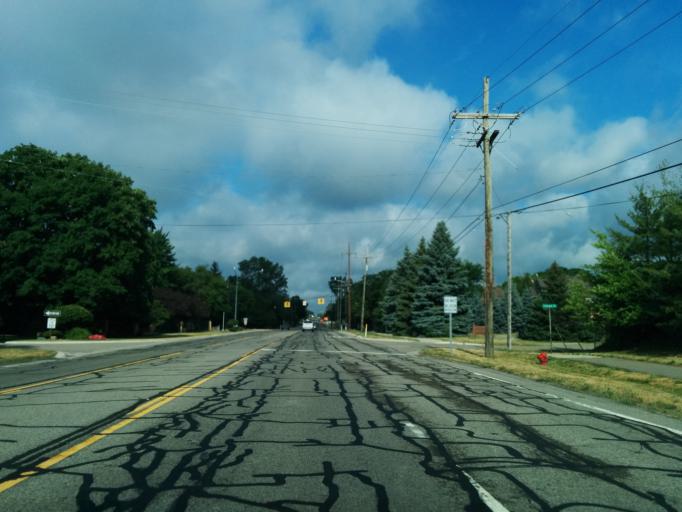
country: US
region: Michigan
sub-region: Oakland County
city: West Bloomfield Township
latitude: 42.5282
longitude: -83.3661
